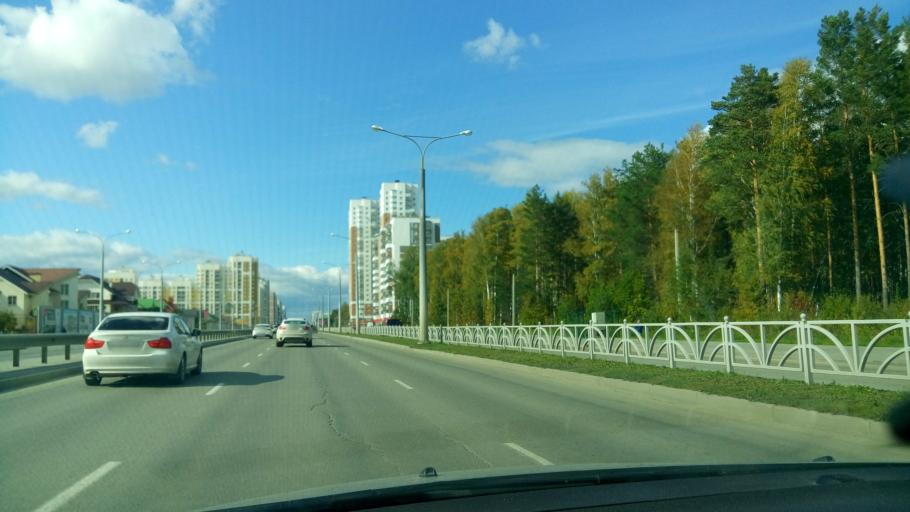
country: RU
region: Sverdlovsk
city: Sovkhoznyy
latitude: 56.7849
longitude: 60.5365
